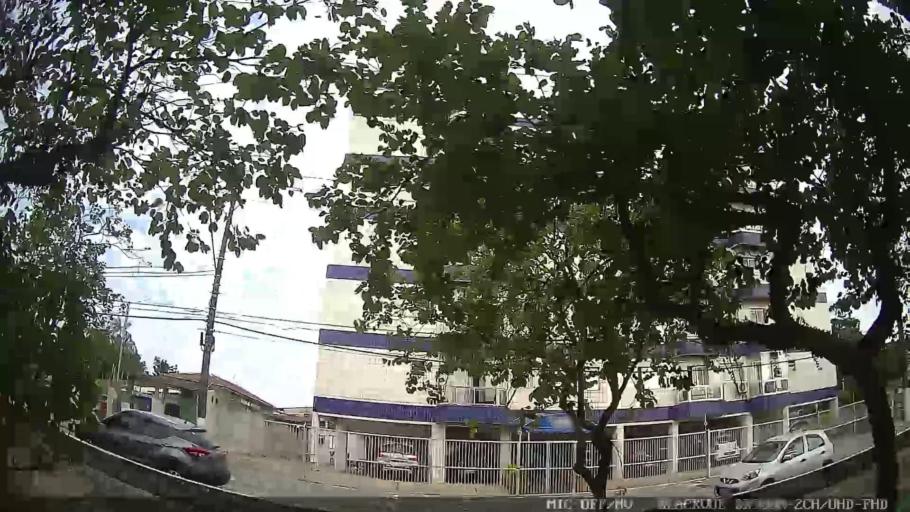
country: BR
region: Sao Paulo
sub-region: Guaruja
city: Guaruja
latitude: -23.9622
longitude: -46.2838
